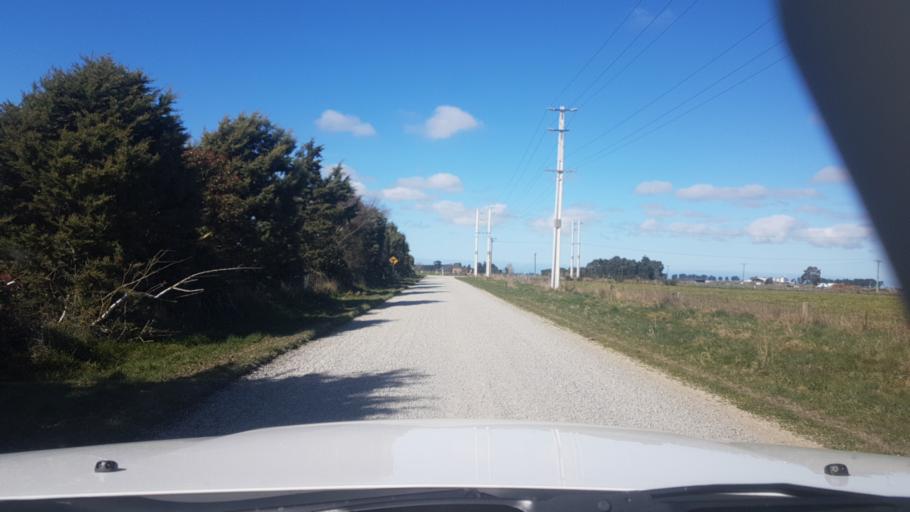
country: NZ
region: Canterbury
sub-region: Timaru District
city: Pleasant Point
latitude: -44.0983
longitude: 171.3887
